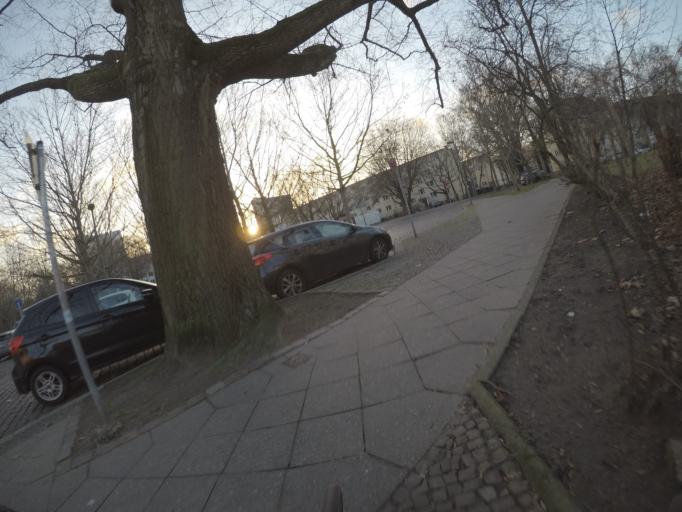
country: DE
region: Berlin
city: Friedrichsfelde
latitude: 52.5023
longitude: 13.5018
